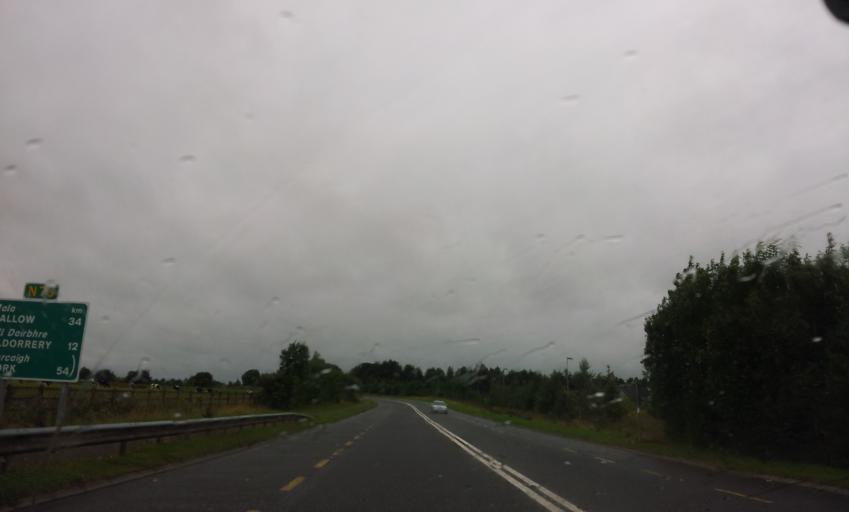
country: IE
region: Munster
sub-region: County Cork
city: Mitchelstown
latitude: 52.2748
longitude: -8.2754
